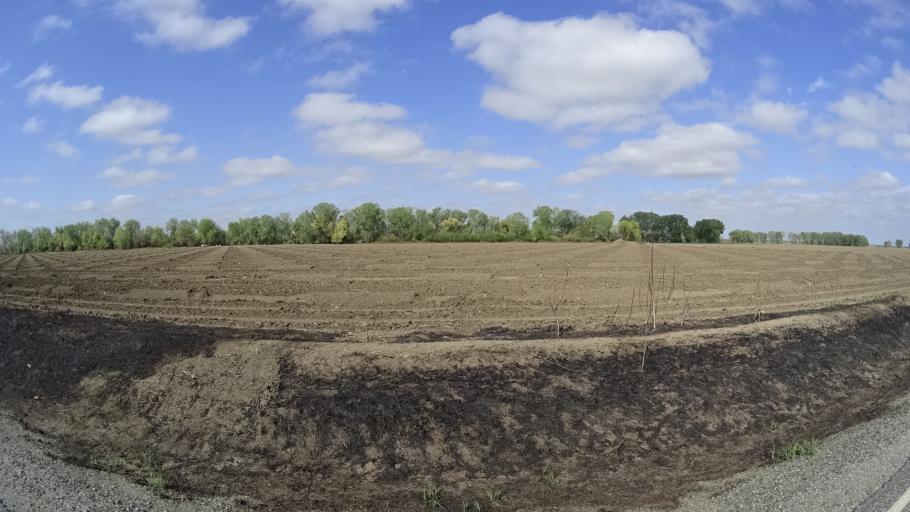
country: US
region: California
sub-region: Colusa County
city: Colusa
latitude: 39.3969
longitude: -121.9286
